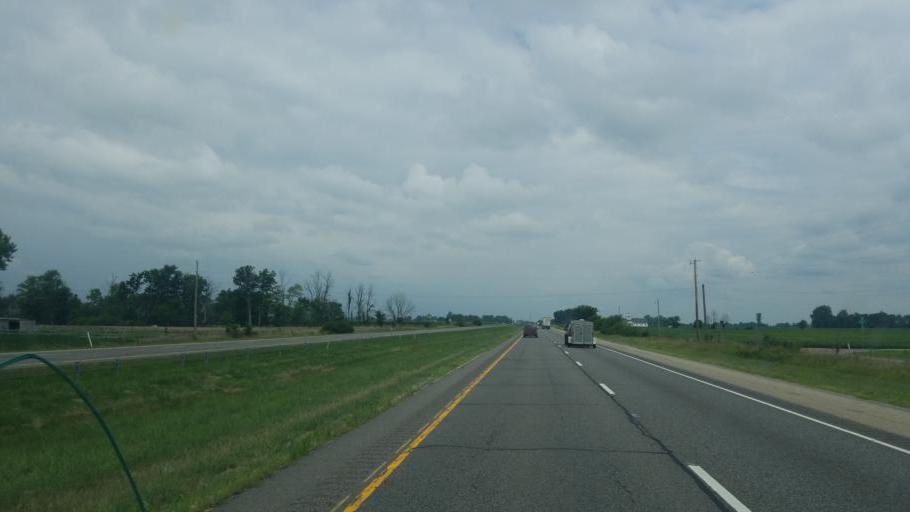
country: US
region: Indiana
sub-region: Madison County
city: Alexandria
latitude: 40.3128
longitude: -85.5585
